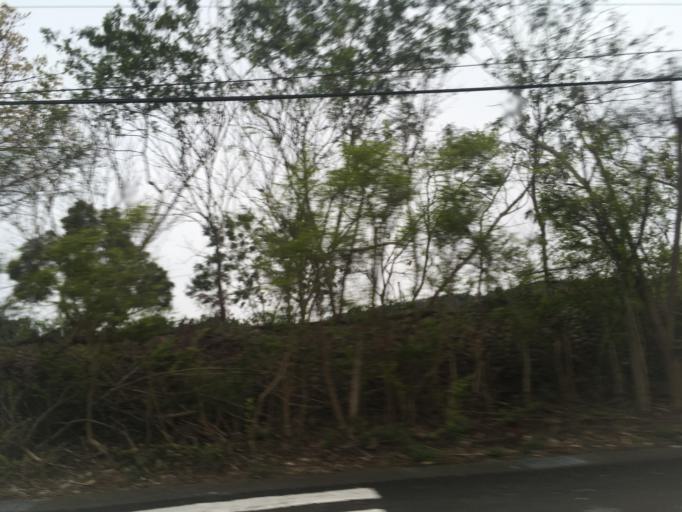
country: TW
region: Taiwan
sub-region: Miaoli
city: Miaoli
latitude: 24.4252
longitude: 120.7275
